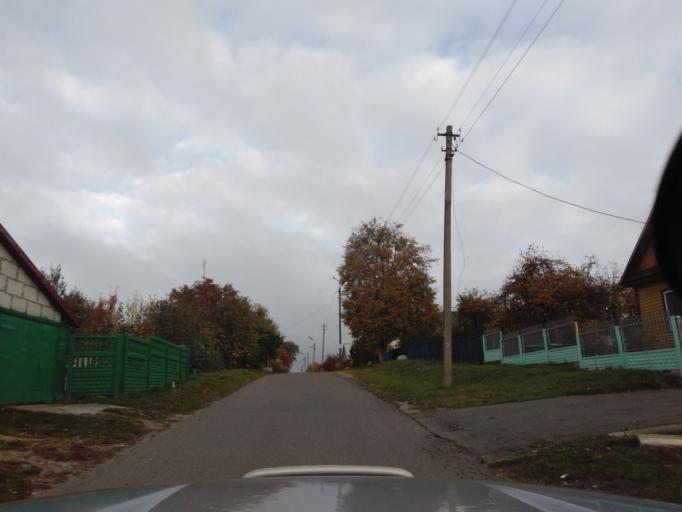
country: BY
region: Minsk
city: Kapyl'
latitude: 53.1581
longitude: 27.0842
